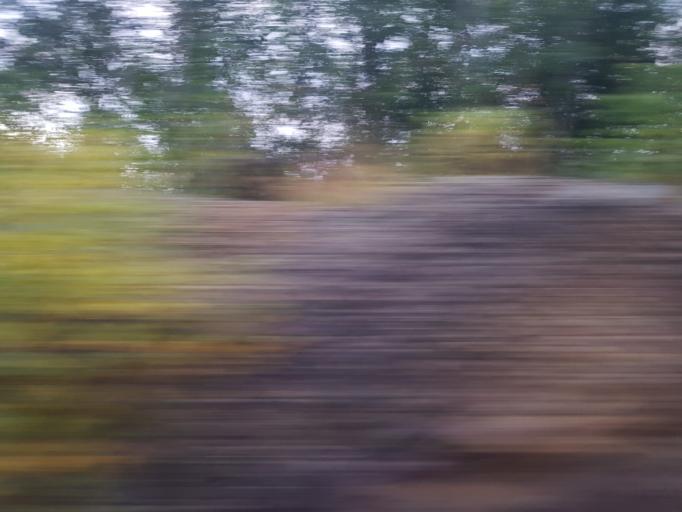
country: NO
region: Sor-Trondelag
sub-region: Trondheim
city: Trondheim
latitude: 63.3774
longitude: 10.3645
